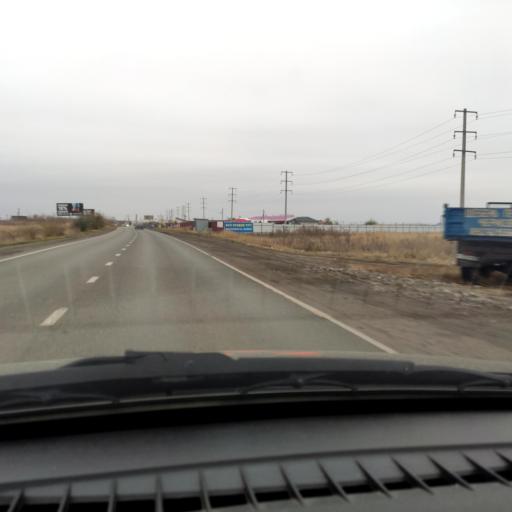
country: RU
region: Samara
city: Podstepki
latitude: 53.5213
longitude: 49.2024
